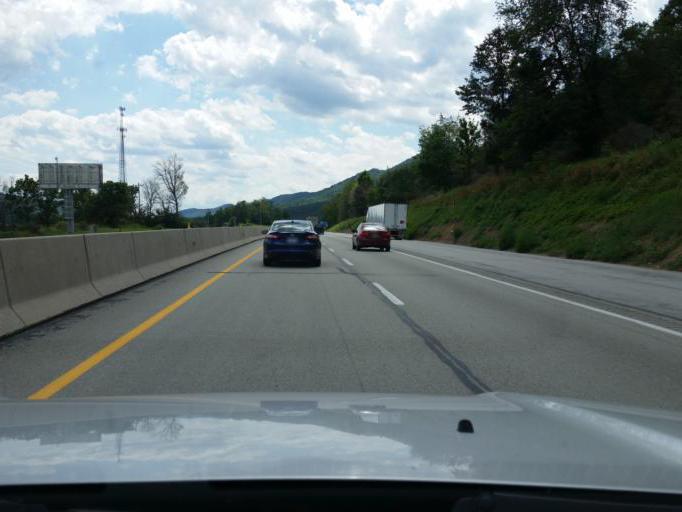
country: US
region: Pennsylvania
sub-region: Franklin County
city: Doylestown
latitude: 40.0820
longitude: -77.8728
